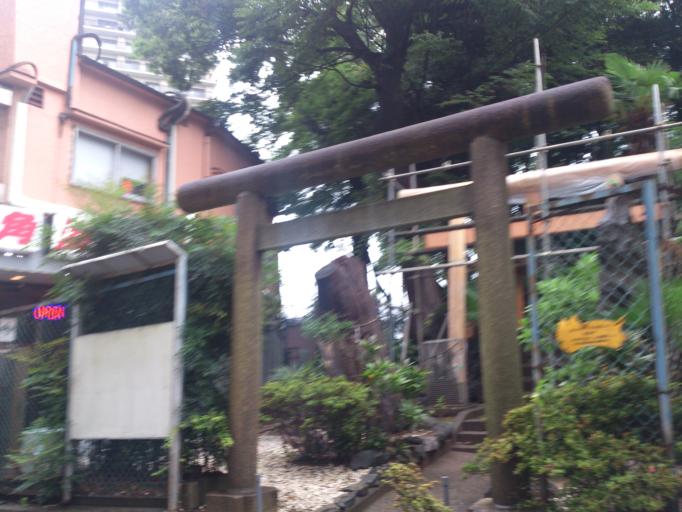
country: JP
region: Chiba
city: Matsudo
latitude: 35.7869
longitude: 139.9020
